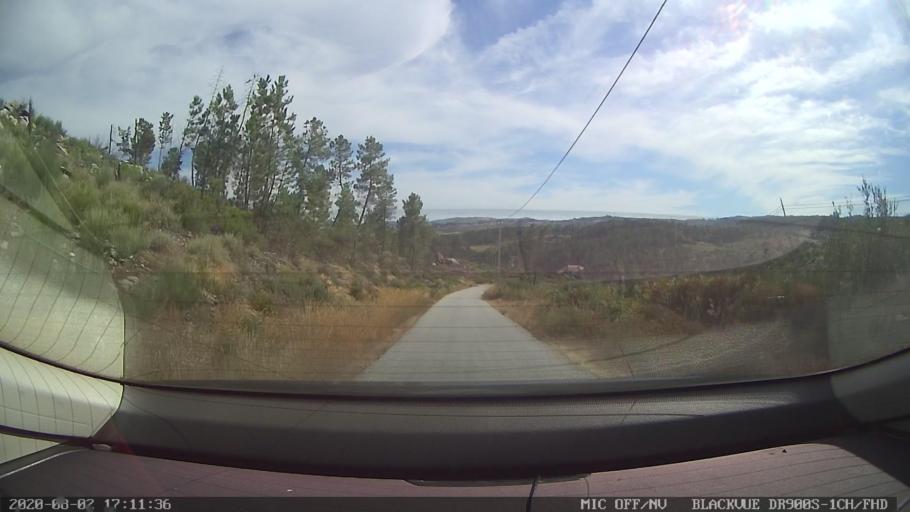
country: PT
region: Vila Real
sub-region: Sabrosa
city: Sabrosa
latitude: 41.3557
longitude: -7.5899
